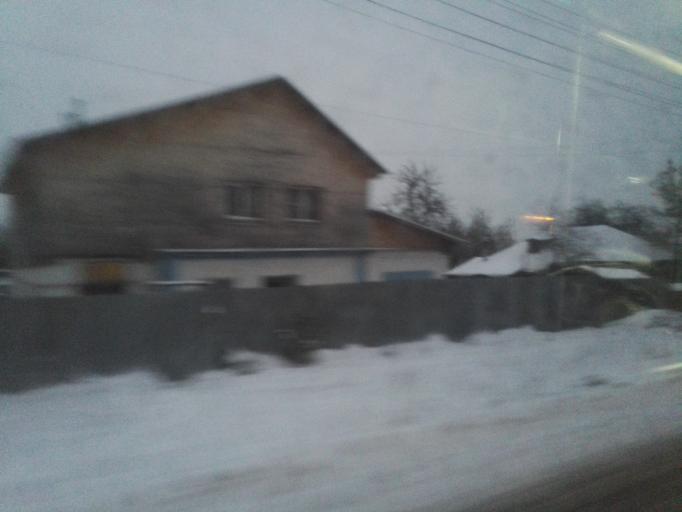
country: RU
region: Tula
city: Tula
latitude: 54.1649
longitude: 37.6074
